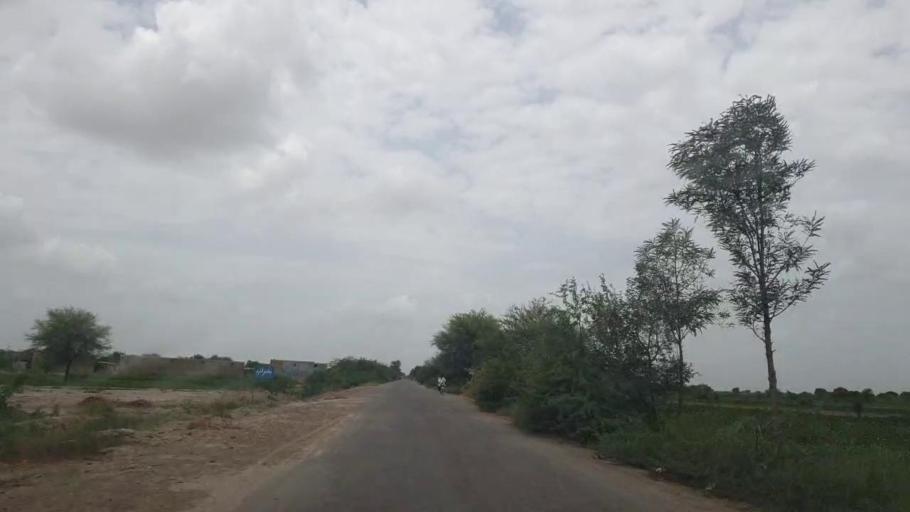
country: PK
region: Sindh
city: Naukot
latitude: 24.8979
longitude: 69.2582
